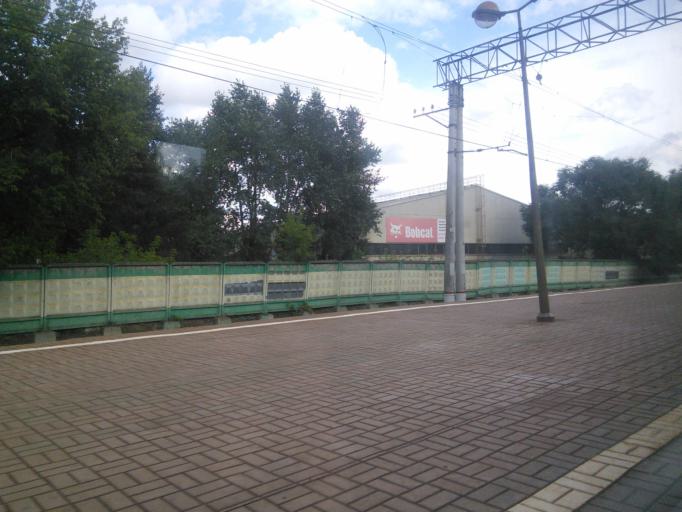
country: RU
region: Moscow
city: Ryazanskiy
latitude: 55.7451
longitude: 37.7391
